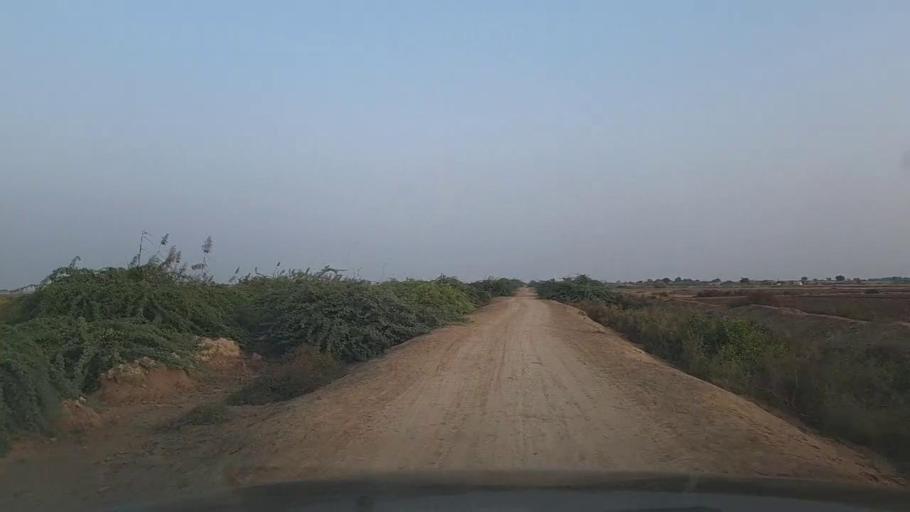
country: PK
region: Sindh
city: Jati
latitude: 24.5430
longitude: 68.3952
